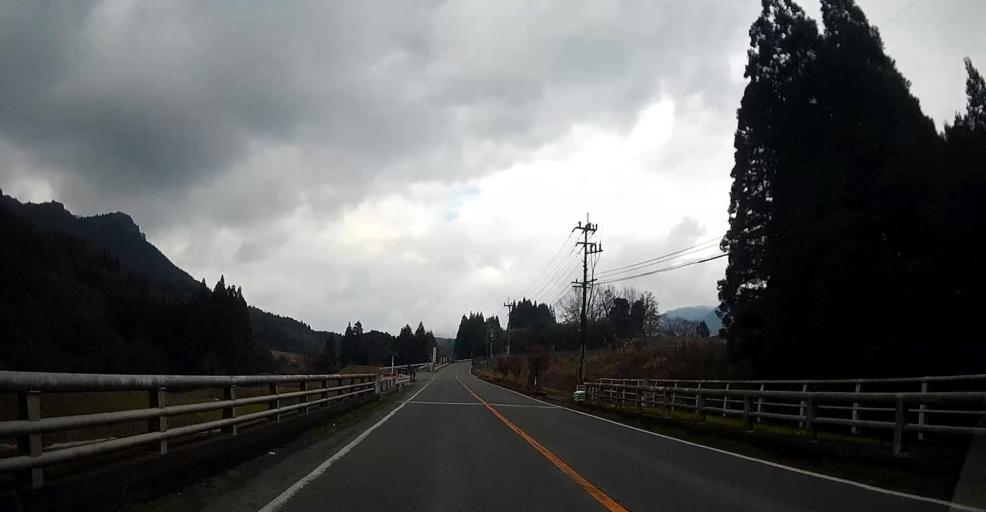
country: JP
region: Kumamoto
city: Matsubase
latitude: 32.6219
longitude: 130.8298
